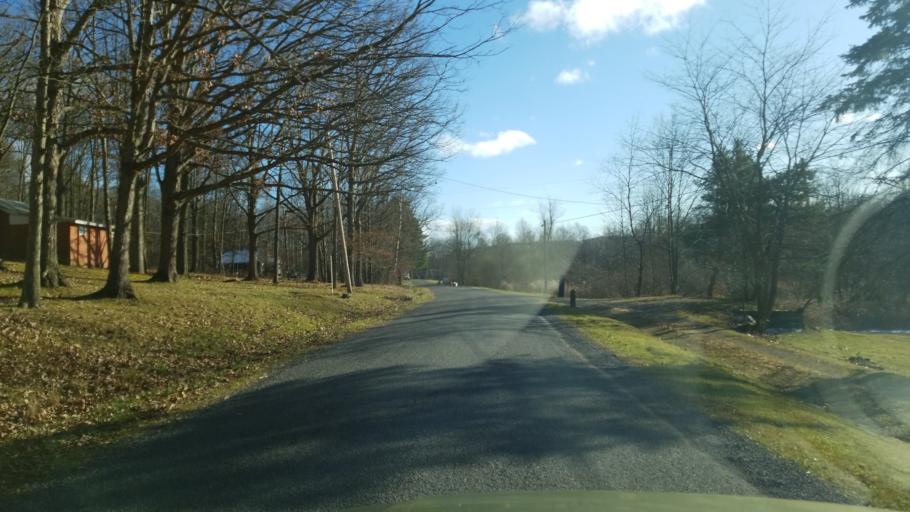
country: US
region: Pennsylvania
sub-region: Jefferson County
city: Brockway
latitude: 41.2646
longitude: -78.8044
